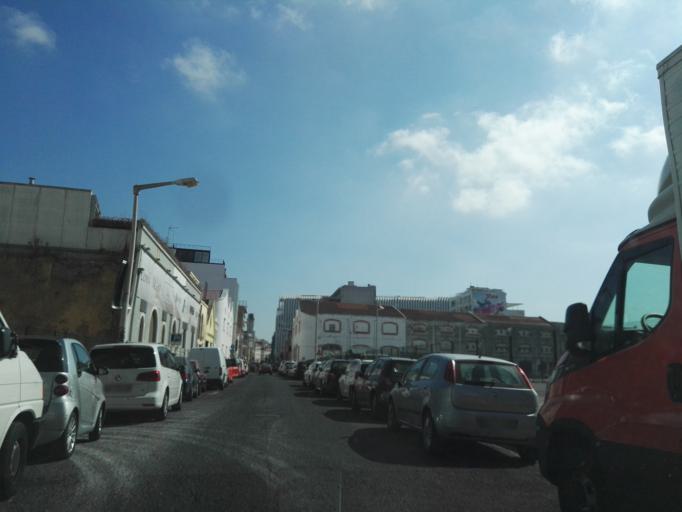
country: PT
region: Setubal
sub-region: Almada
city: Cacilhas
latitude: 38.7076
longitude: -9.1524
